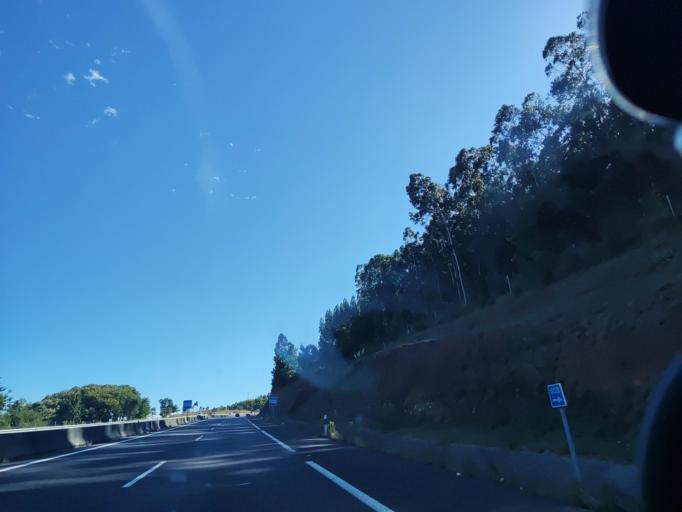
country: ES
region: Galicia
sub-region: Provincia da Coruna
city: Boiro
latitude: 42.6500
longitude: -8.9028
